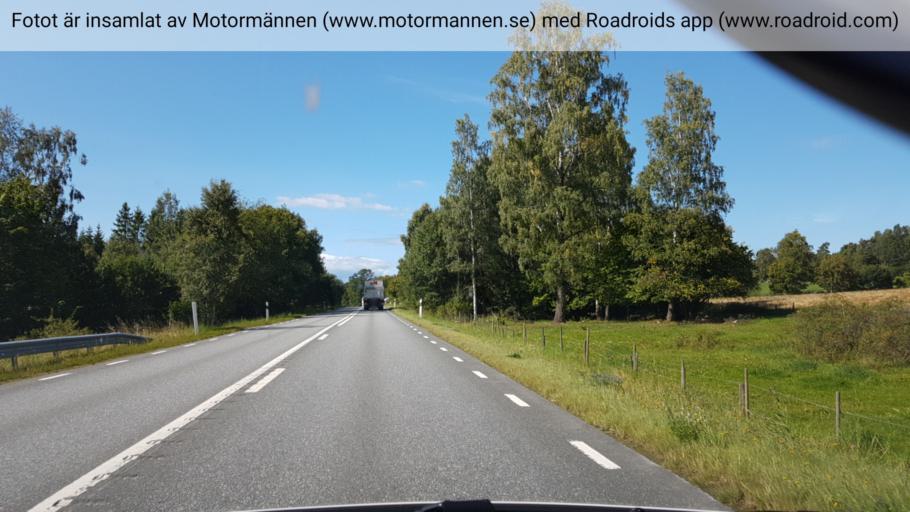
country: SE
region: Joenkoeping
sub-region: Jonkopings Kommun
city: Asa
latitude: 58.0029
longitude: 14.6084
